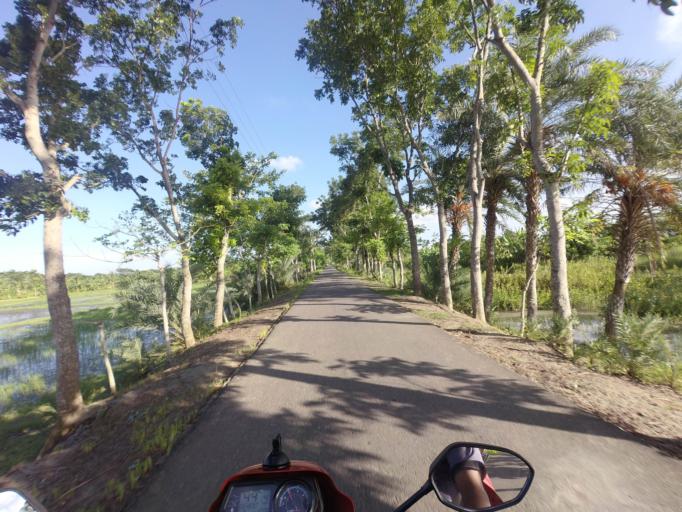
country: BD
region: Khulna
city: Bhatpara Abhaynagar
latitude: 22.9373
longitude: 89.5214
